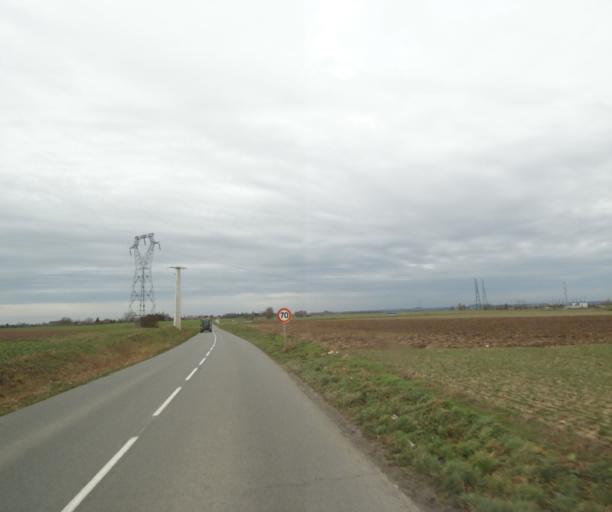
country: FR
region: Nord-Pas-de-Calais
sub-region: Departement du Nord
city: Curgies
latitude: 50.3540
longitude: 3.6154
